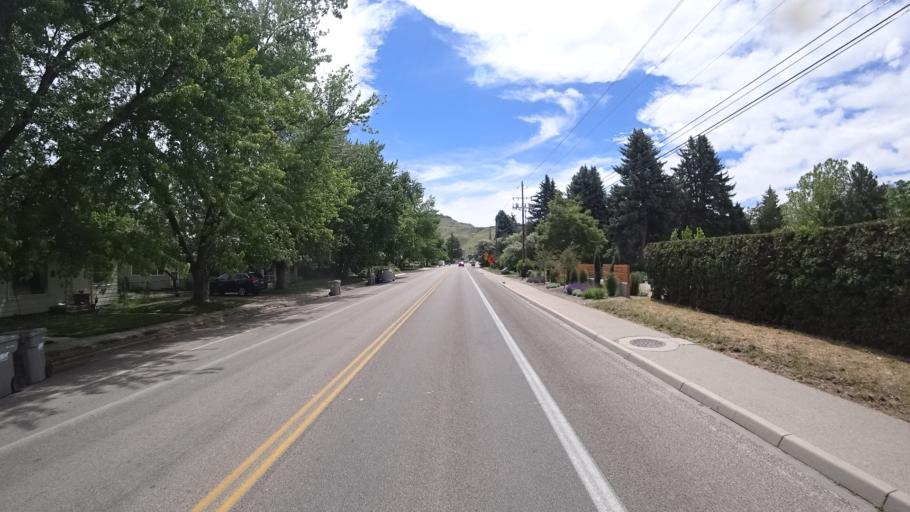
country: US
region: Idaho
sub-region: Ada County
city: Boise
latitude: 43.6018
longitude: -116.1701
